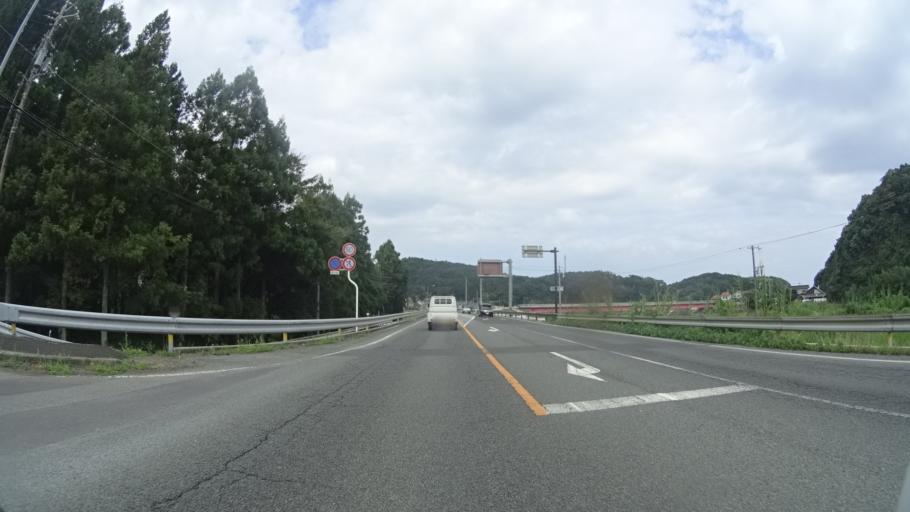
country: JP
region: Shimane
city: Odacho-oda
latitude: 35.1989
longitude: 132.4710
